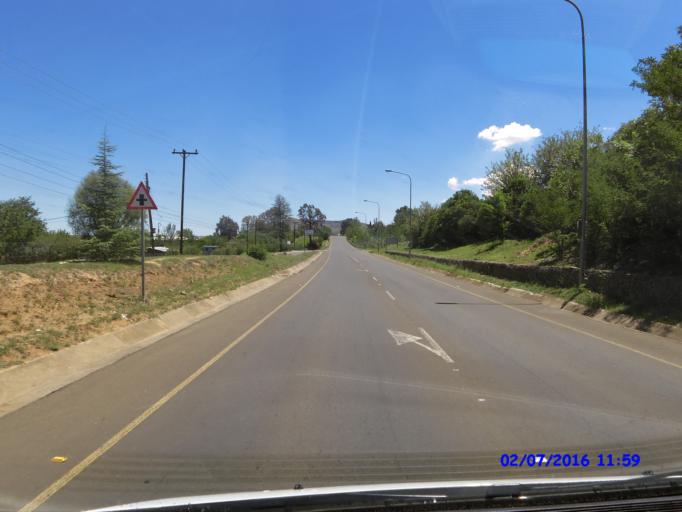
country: LS
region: Maseru
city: Maseru
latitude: -29.3139
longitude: 27.4697
